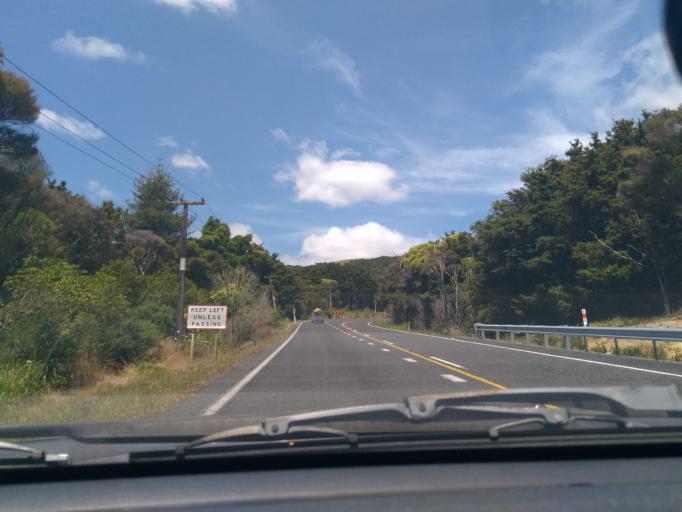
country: NZ
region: Northland
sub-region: Far North District
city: Kerikeri
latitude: -35.1179
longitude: 173.8184
